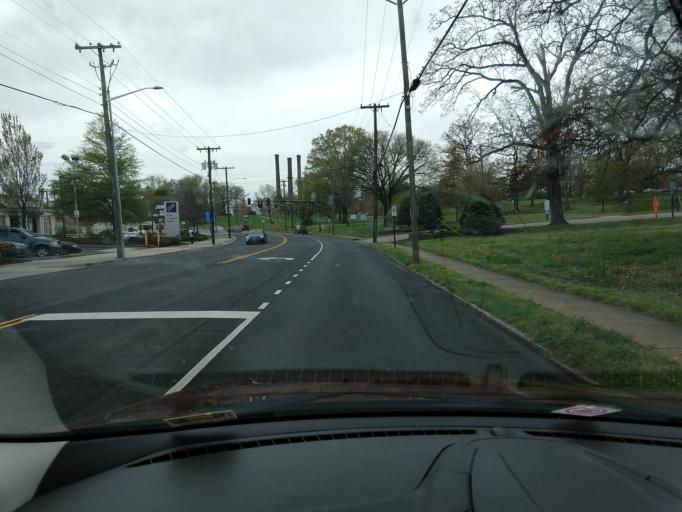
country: US
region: Virginia
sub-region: City of Danville
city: Danville
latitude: 36.5724
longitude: -79.4198
